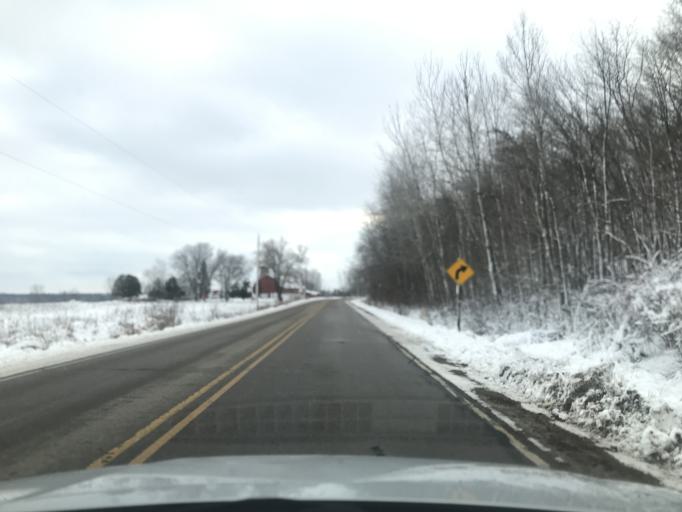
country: US
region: Wisconsin
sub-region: Oconto County
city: Oconto
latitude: 44.9429
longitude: -87.9867
